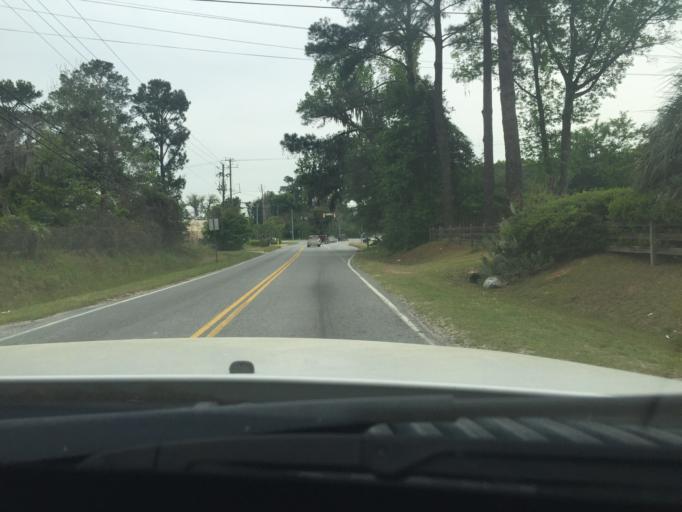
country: US
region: Georgia
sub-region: Chatham County
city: Georgetown
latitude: 31.9960
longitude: -81.2589
